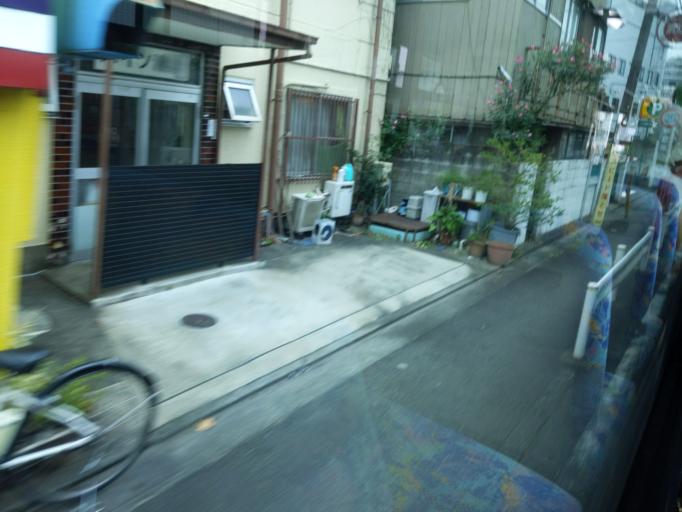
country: JP
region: Kanagawa
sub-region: Kawasaki-shi
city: Kawasaki
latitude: 35.5870
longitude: 139.6956
